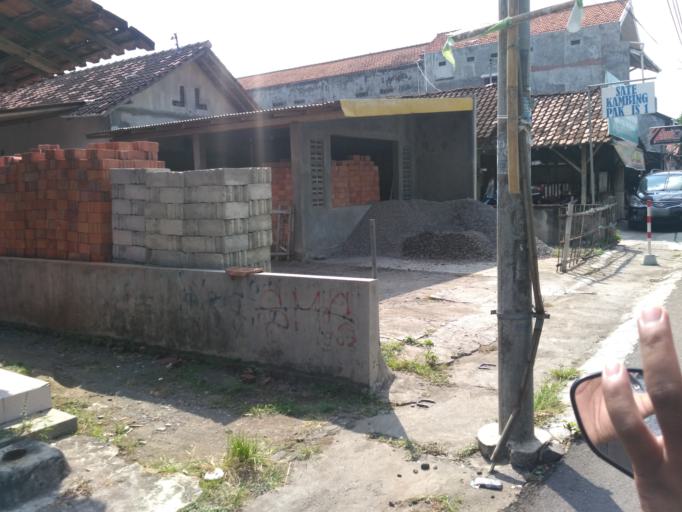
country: ID
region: Daerah Istimewa Yogyakarta
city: Depok
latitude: -7.7802
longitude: 110.4085
